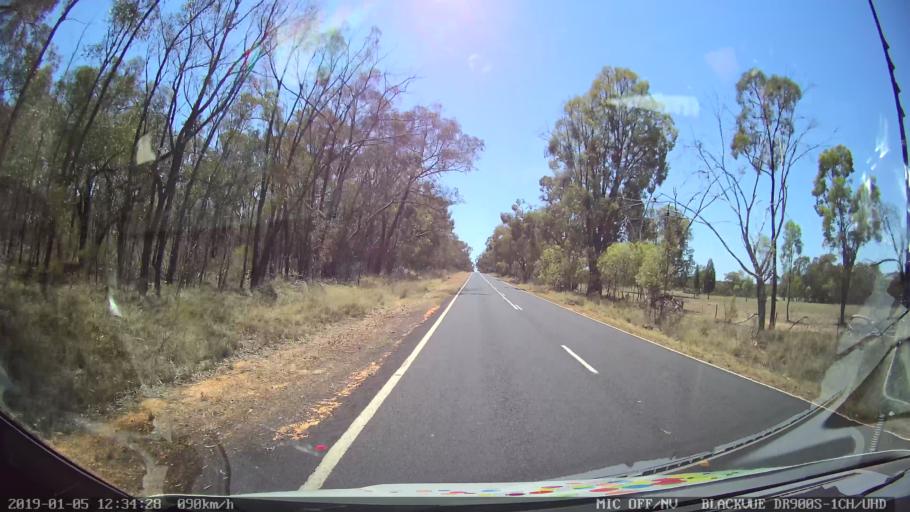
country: AU
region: New South Wales
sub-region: Warrumbungle Shire
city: Coonabarabran
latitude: -31.2120
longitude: 149.4109
